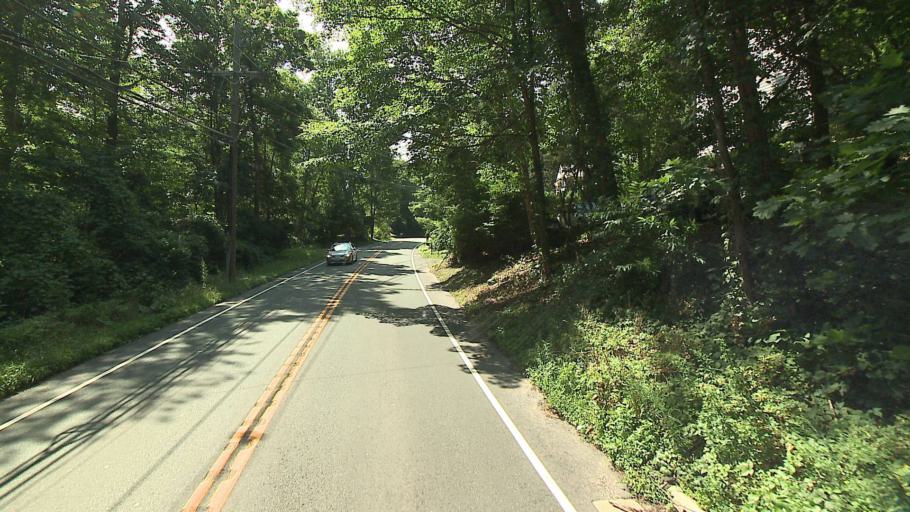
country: US
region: New York
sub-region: Putnam County
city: Putnam Lake
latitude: 41.4759
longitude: -73.4676
